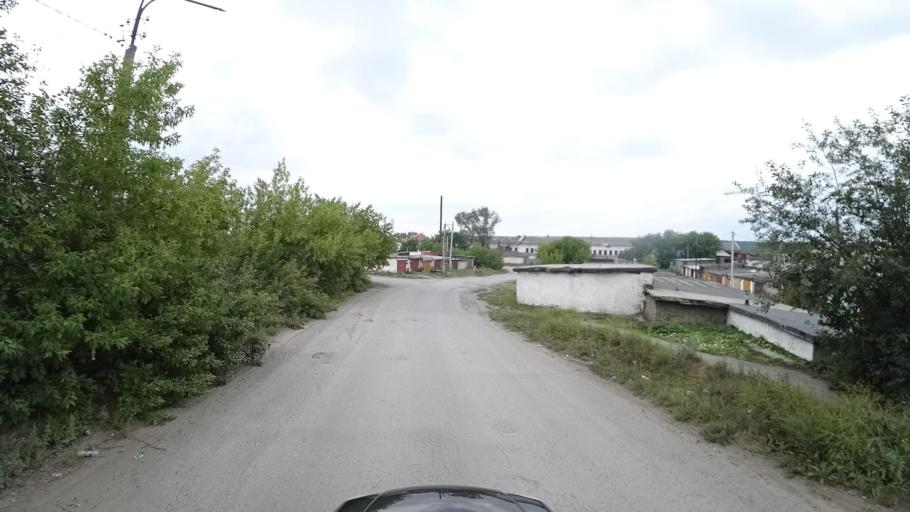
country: RU
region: Sverdlovsk
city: Kamyshlov
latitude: 56.8349
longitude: 62.7193
